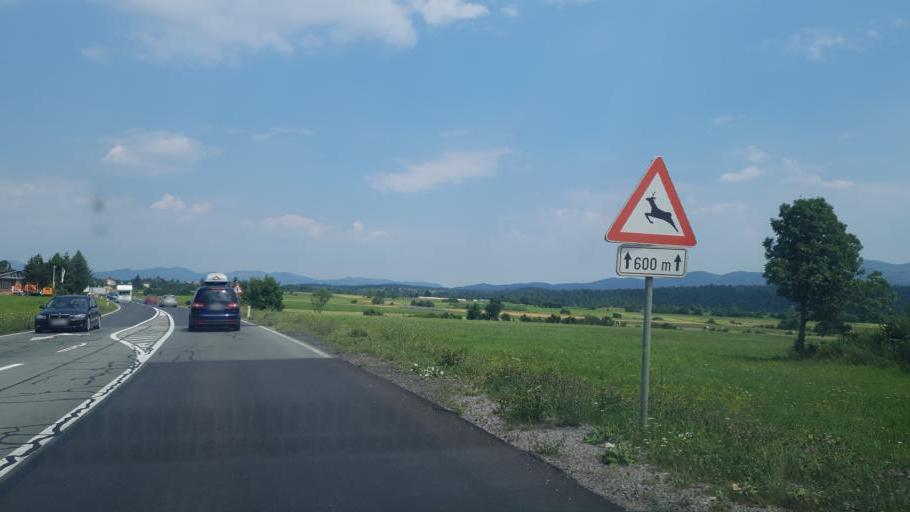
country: SI
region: Pivka
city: Pivka
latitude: 45.6941
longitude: 14.1946
